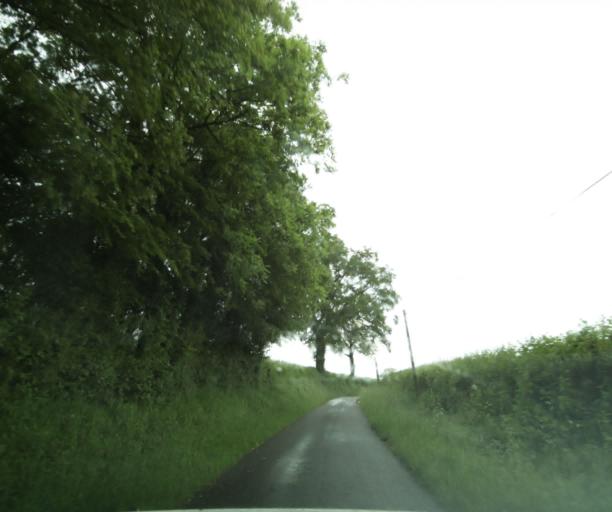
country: FR
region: Bourgogne
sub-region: Departement de Saone-et-Loire
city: Ciry-le-Noble
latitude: 46.5363
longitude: 4.3600
